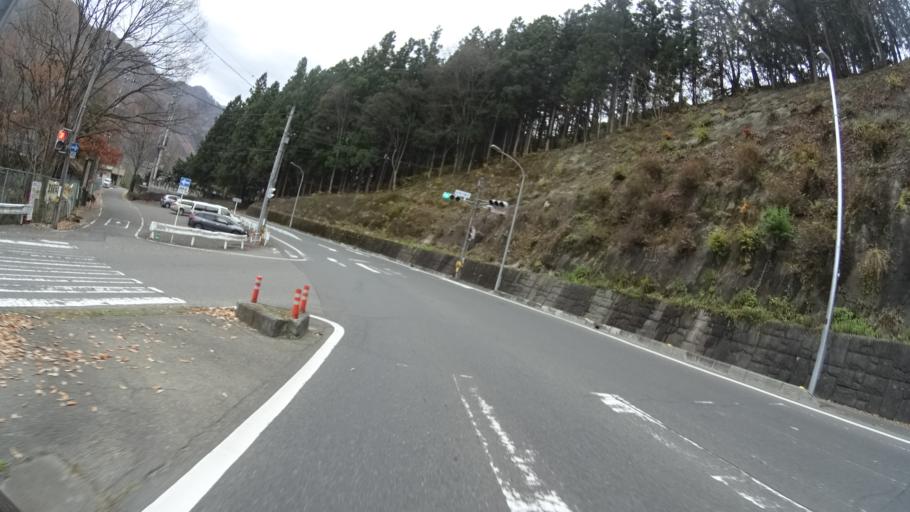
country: JP
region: Gunma
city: Numata
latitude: 36.6979
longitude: 139.2082
